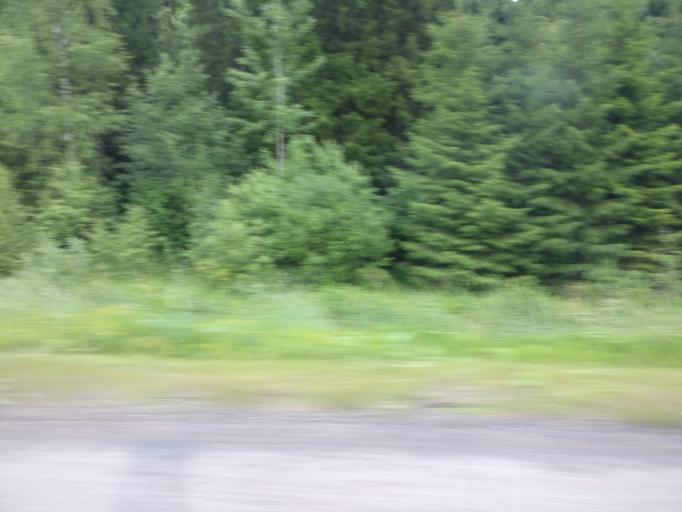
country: FI
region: Northern Savo
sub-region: Varkaus
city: Leppaevirta
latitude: 62.4409
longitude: 27.8037
